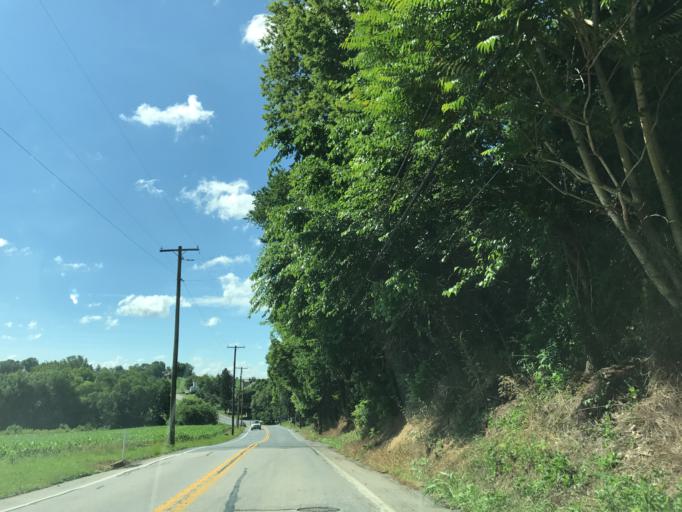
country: US
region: Pennsylvania
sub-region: Lancaster County
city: Elizabethtown
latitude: 40.1333
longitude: -76.5997
